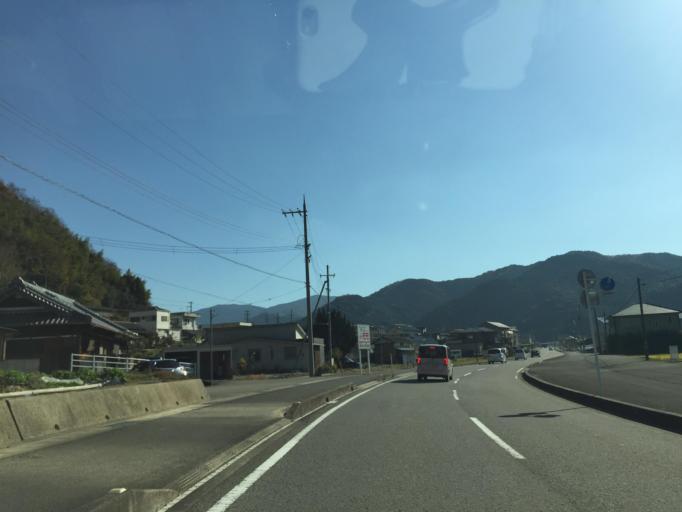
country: JP
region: Wakayama
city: Iwade
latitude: 34.1602
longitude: 135.3102
